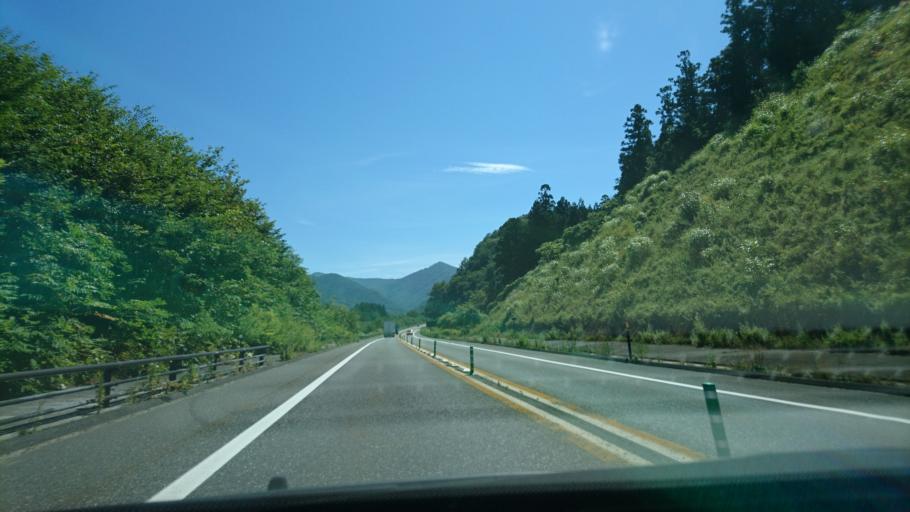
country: JP
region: Iwate
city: Tono
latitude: 39.2629
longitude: 141.6081
